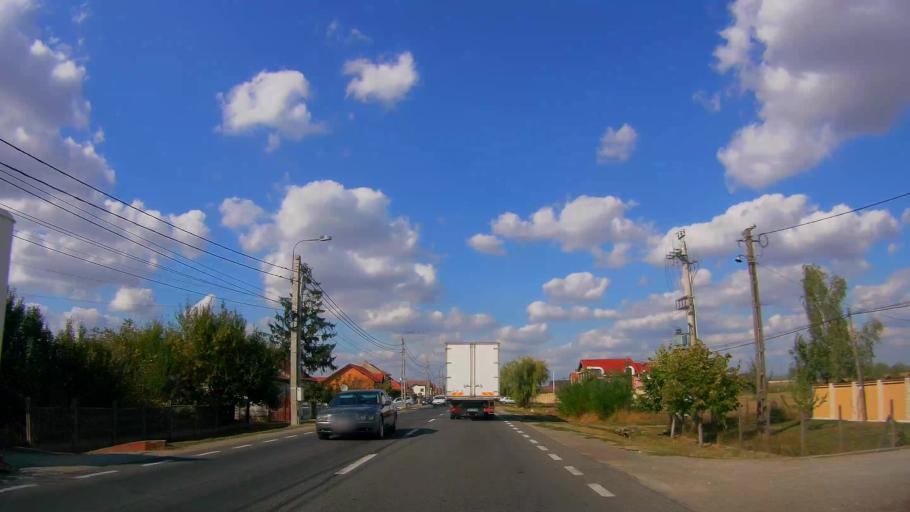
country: RO
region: Satu Mare
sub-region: Comuna Paulesti
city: Paulesti
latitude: 47.7431
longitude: 22.8828
